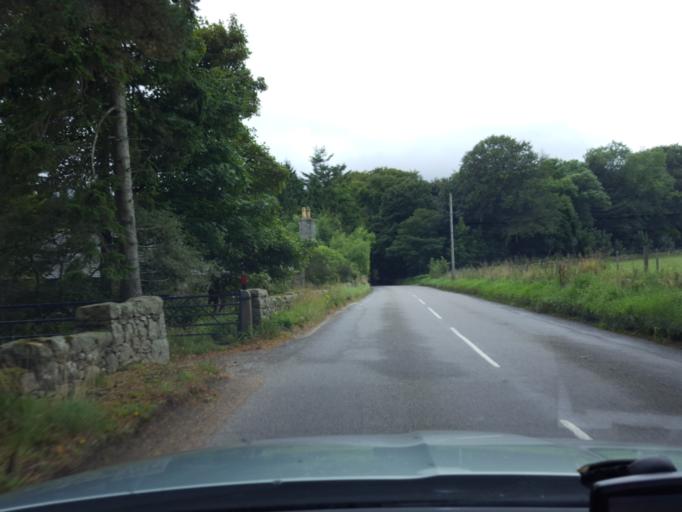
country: GB
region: Scotland
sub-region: Aberdeenshire
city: Kemnay
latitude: 57.1668
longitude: -2.4231
